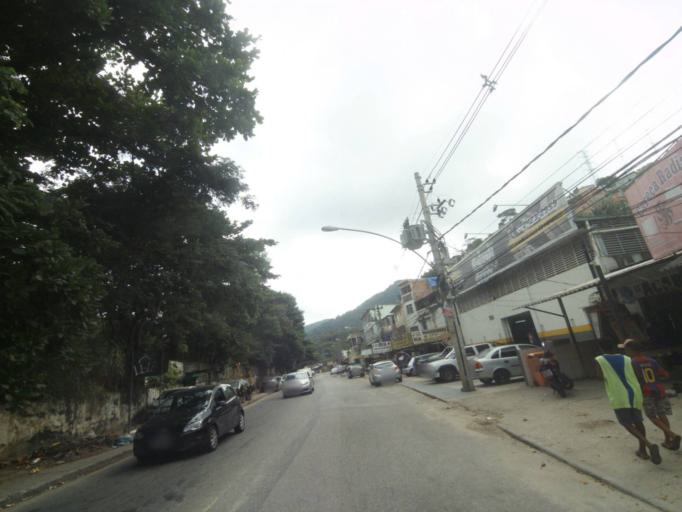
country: BR
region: Rio de Janeiro
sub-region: Sao Joao De Meriti
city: Sao Joao de Meriti
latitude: -22.9070
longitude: -43.3803
